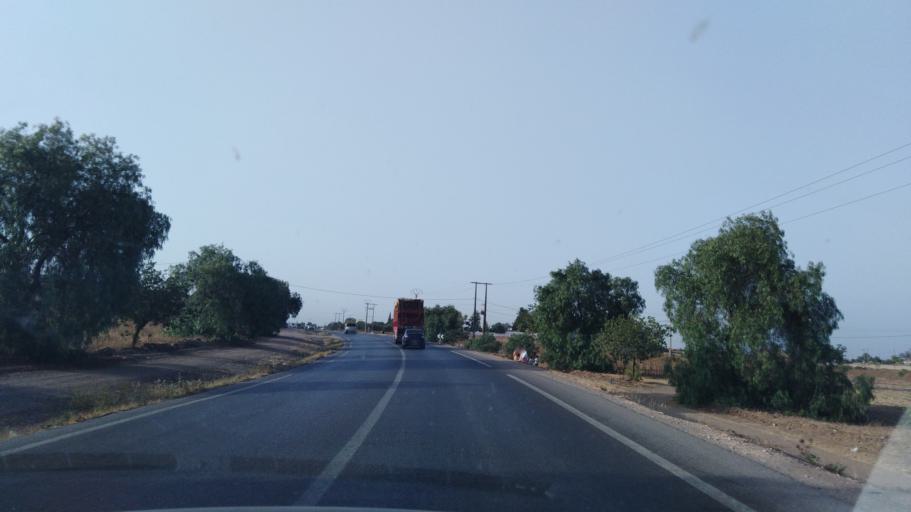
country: MA
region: Chaouia-Ouardigha
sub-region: Settat Province
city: Berrechid
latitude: 33.2328
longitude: -7.5894
